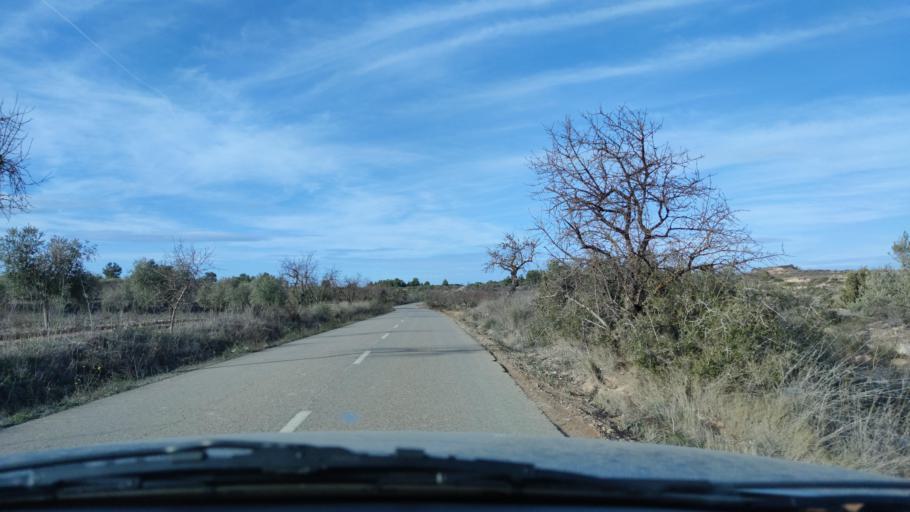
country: ES
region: Catalonia
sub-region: Provincia de Lleida
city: el Cogul
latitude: 41.4665
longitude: 0.6799
